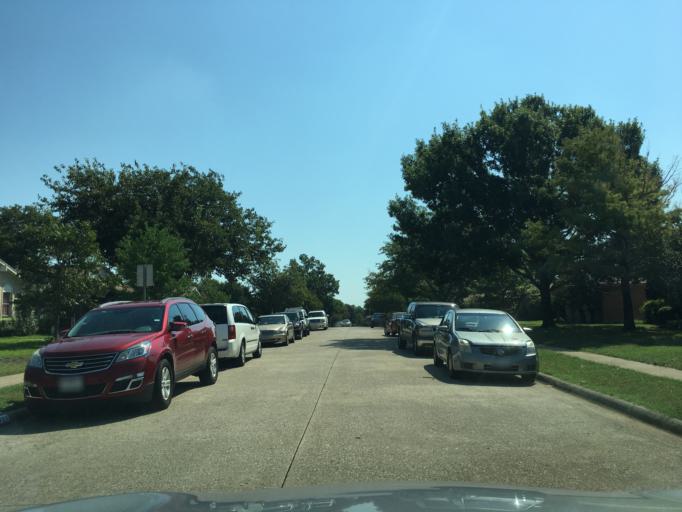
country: US
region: Texas
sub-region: Dallas County
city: Garland
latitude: 32.9339
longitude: -96.6538
